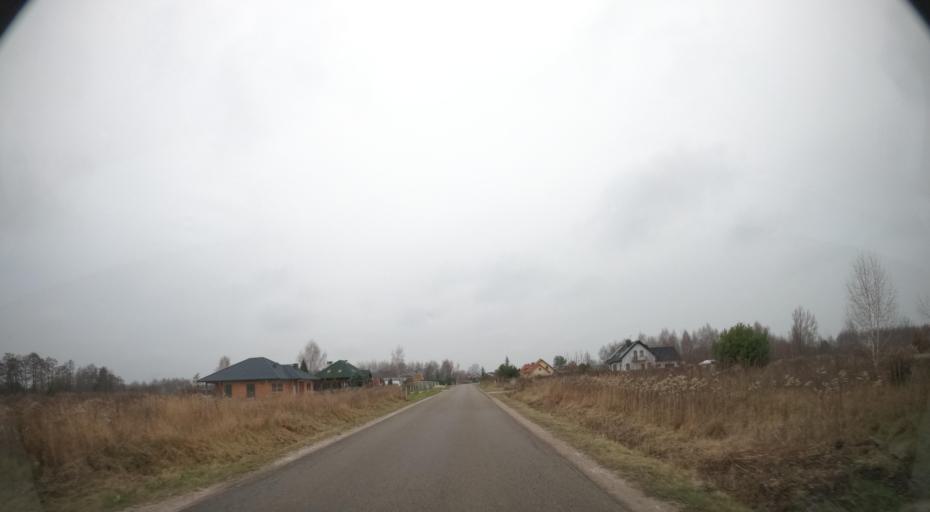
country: PL
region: Masovian Voivodeship
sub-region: Powiat radomski
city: Skaryszew
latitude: 51.3792
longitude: 21.2406
